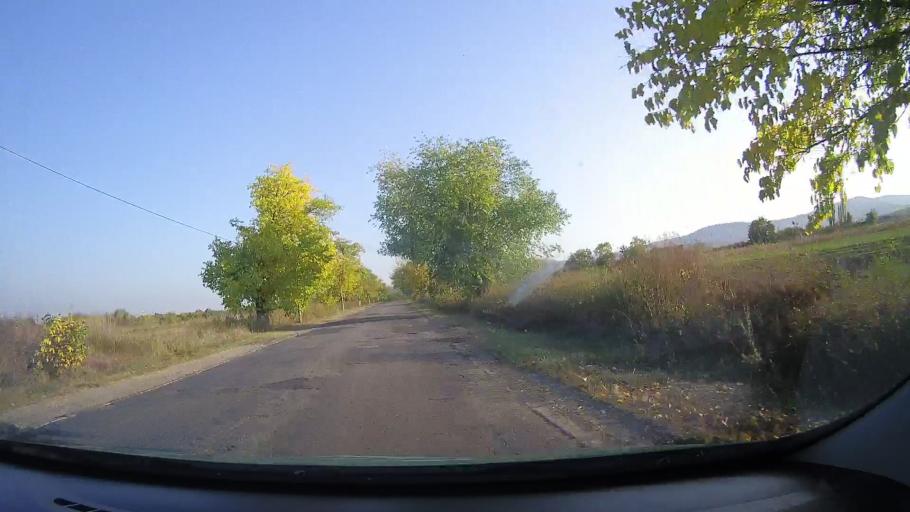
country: RO
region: Arad
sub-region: Comuna Pancota
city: Maderat
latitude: 46.3066
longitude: 21.7078
